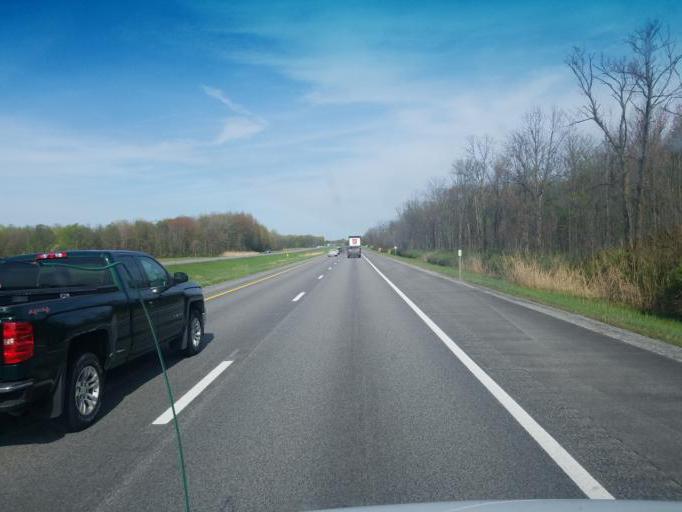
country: US
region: New York
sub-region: Madison County
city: Bolivar
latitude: 43.0911
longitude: -75.9212
